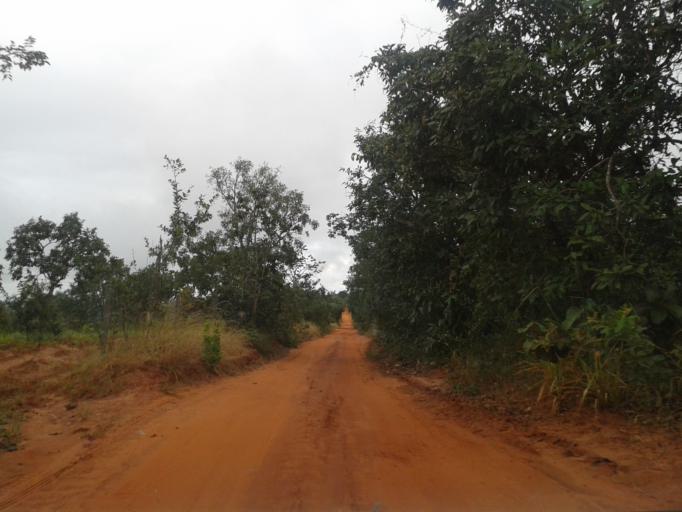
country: BR
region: Minas Gerais
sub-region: Campina Verde
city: Campina Verde
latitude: -19.3965
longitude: -49.6185
